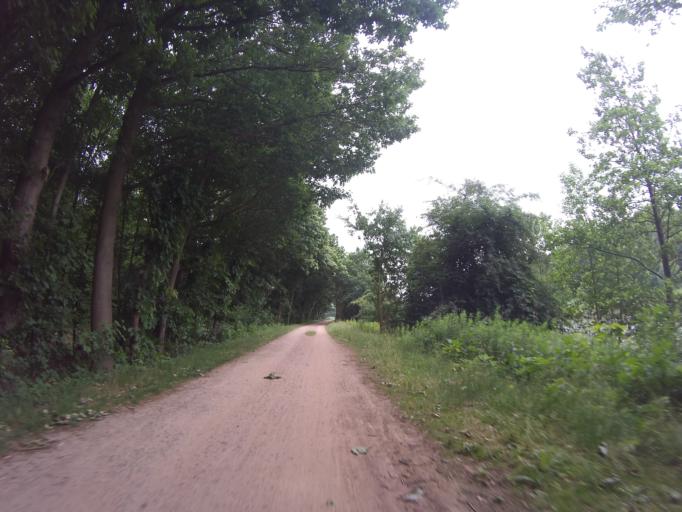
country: DE
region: Lower Saxony
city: Meppen
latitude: 52.7135
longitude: 7.2778
